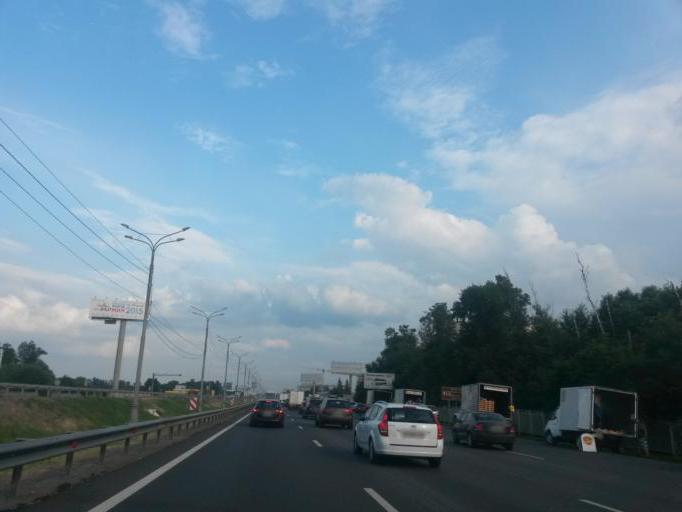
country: RU
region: Moskovskaya
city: Razvilka
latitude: 55.5876
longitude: 37.7354
